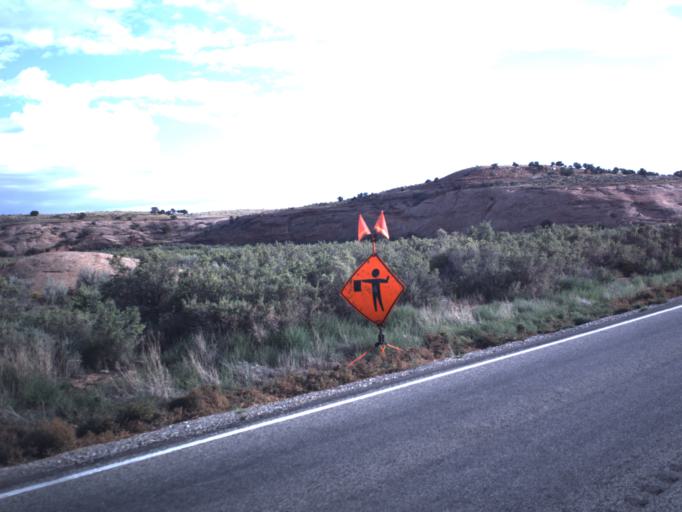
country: US
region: Utah
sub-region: San Juan County
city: Monticello
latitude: 38.1957
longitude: -109.3768
